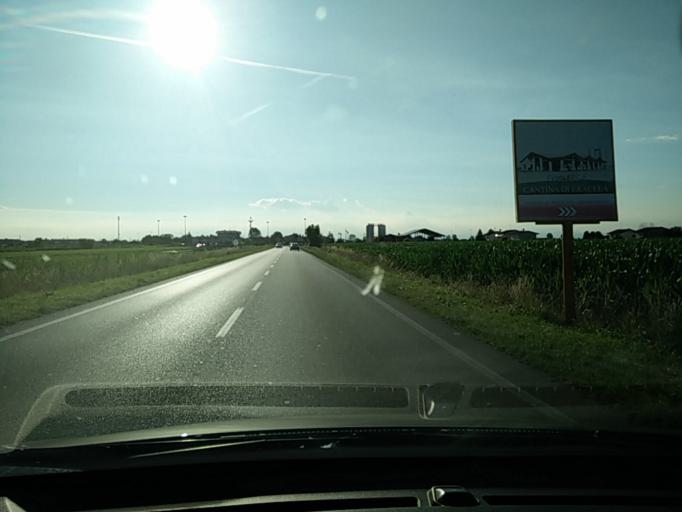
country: IT
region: Veneto
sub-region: Provincia di Venezia
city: Crepaldo
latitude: 45.5770
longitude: 12.6937
